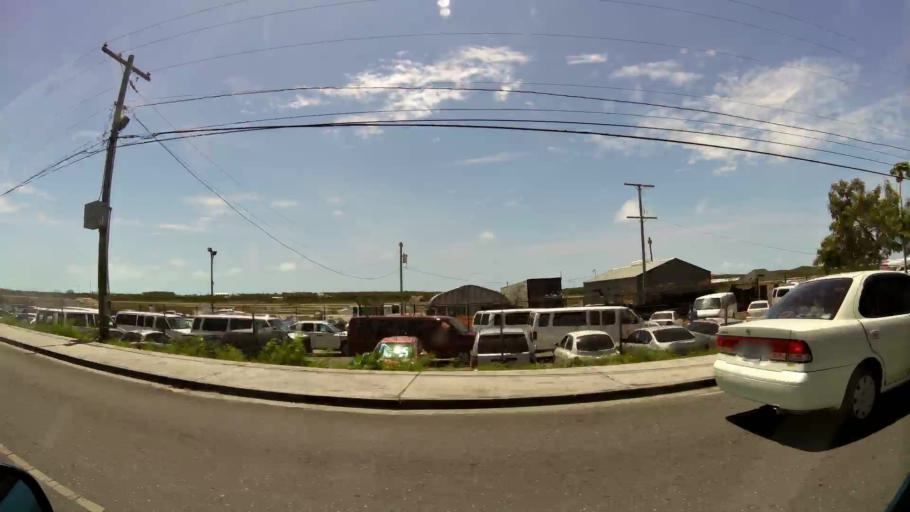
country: BS
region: Mayaguana
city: Abraham's Bay
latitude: 21.7763
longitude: -72.2694
